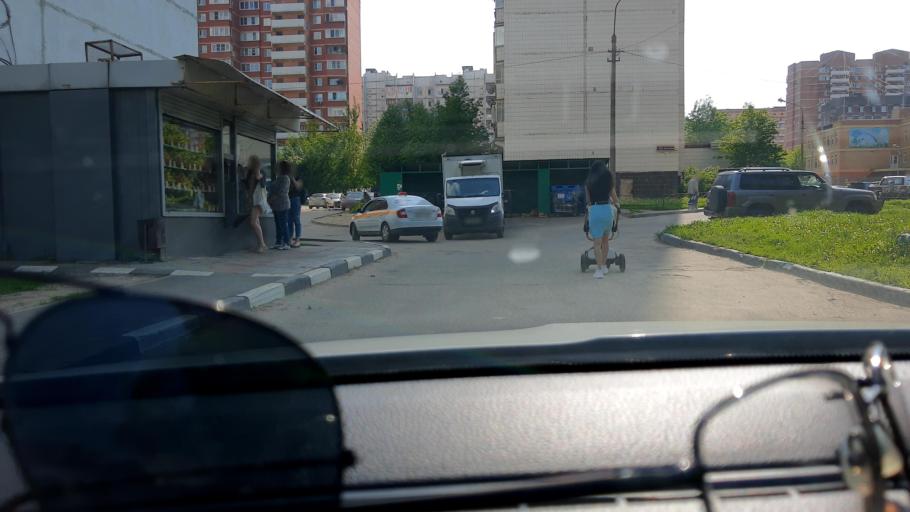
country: RU
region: Moskovskaya
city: Lobnya
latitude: 56.0202
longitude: 37.4286
